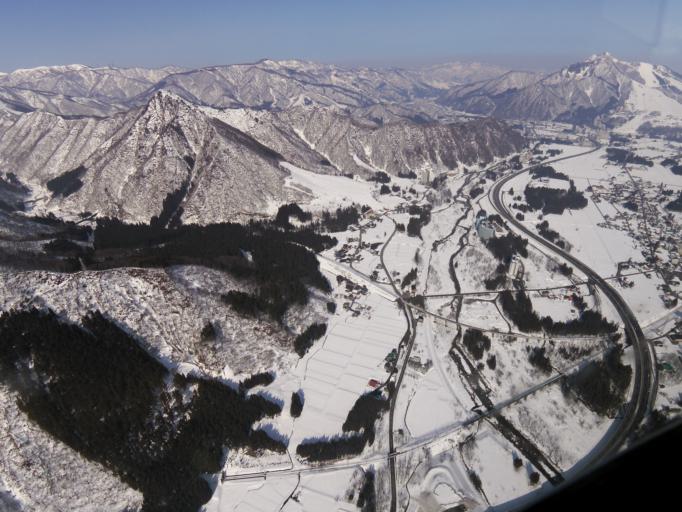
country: JP
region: Niigata
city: Shiozawa
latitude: 36.8971
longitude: 138.8469
